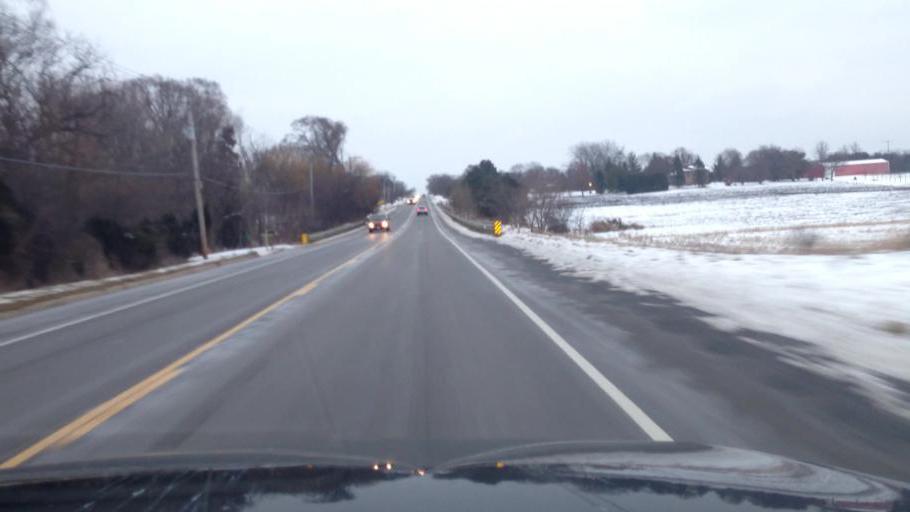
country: US
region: Illinois
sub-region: McHenry County
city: Woodstock
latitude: 42.2550
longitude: -88.4683
